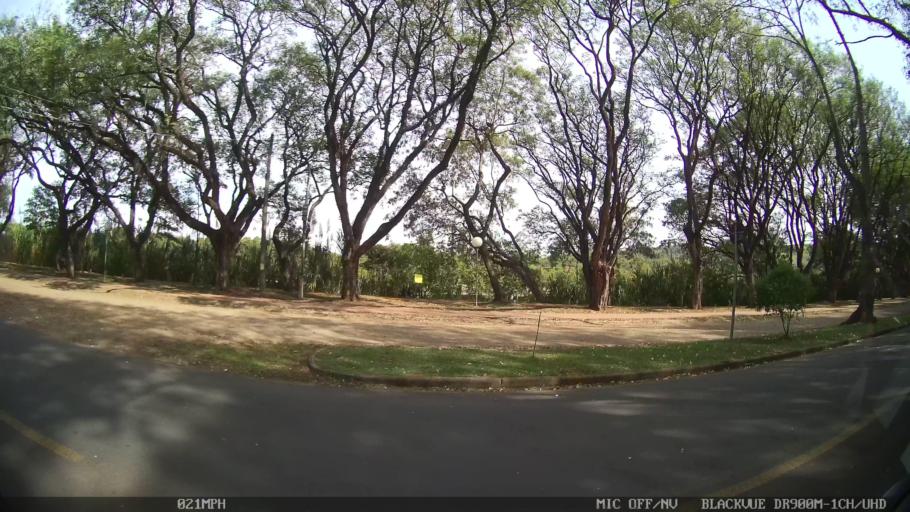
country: BR
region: Sao Paulo
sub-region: Piracicaba
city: Piracicaba
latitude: -22.7203
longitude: -47.6728
